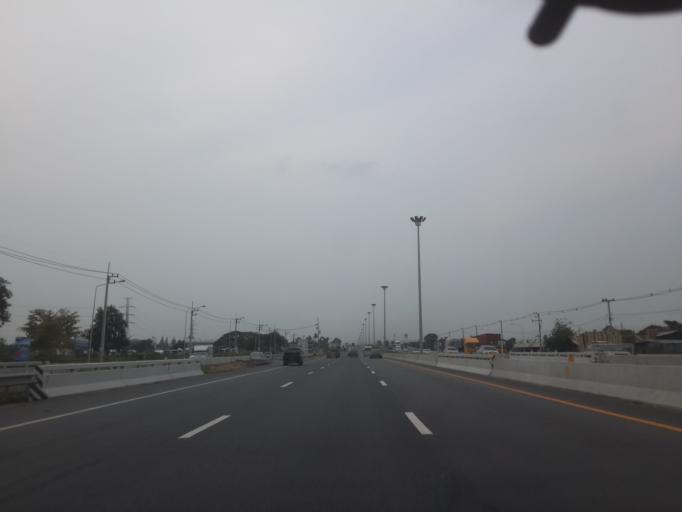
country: TH
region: Chon Buri
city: Ban Talat Bueng
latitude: 13.0730
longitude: 100.9942
